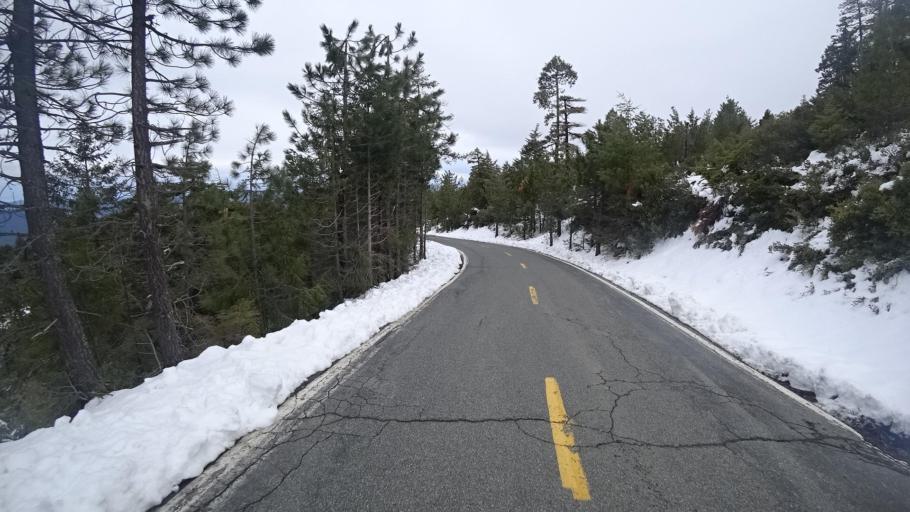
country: US
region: California
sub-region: Humboldt County
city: Willow Creek
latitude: 40.8646
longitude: -123.7381
